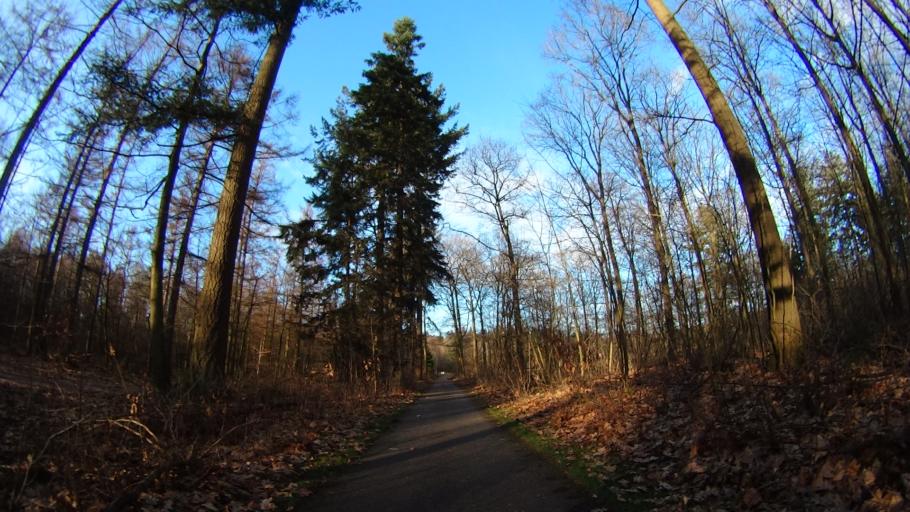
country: NL
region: Drenthe
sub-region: Gemeente Coevorden
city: Sleen
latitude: 52.8128
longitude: 6.7709
